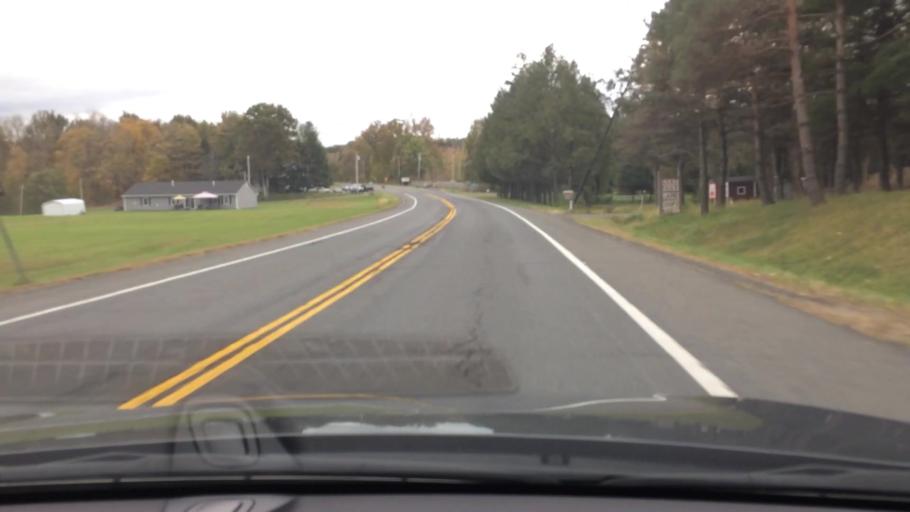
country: US
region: New York
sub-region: Columbia County
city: Oakdale
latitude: 42.1471
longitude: -73.7450
